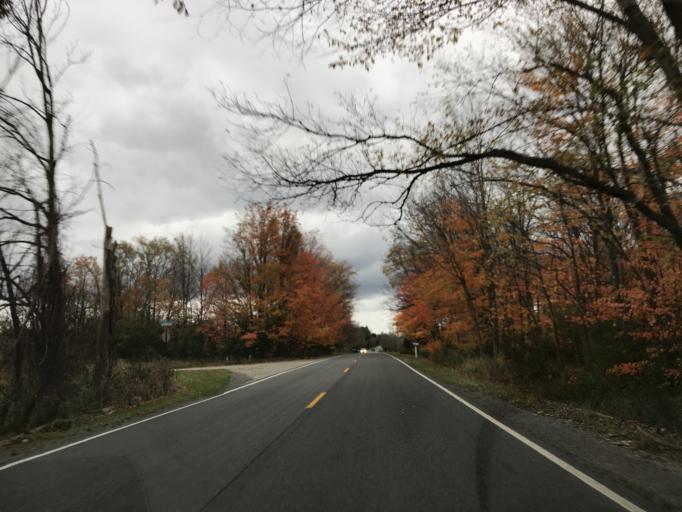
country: US
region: Michigan
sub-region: Washtenaw County
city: Ann Arbor
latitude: 42.3388
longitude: -83.7174
